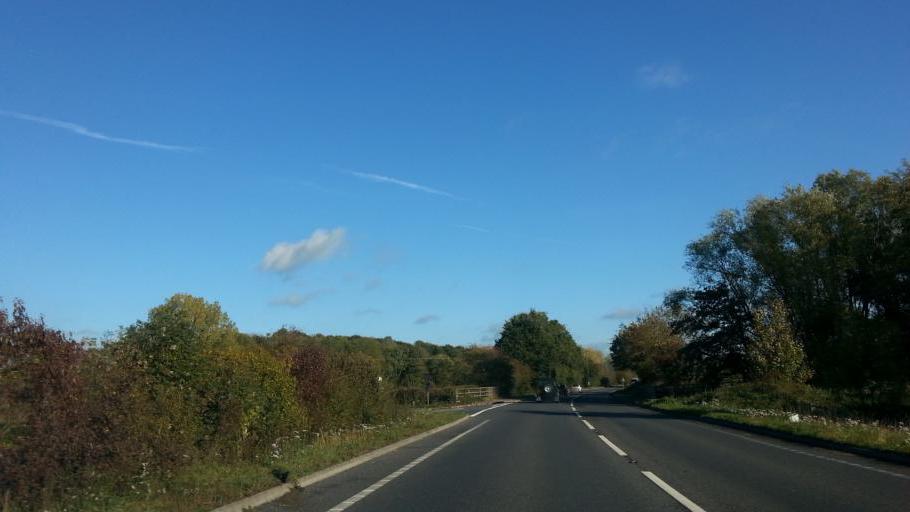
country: GB
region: England
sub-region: Norfolk
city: Harleston
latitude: 52.4126
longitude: 1.3261
